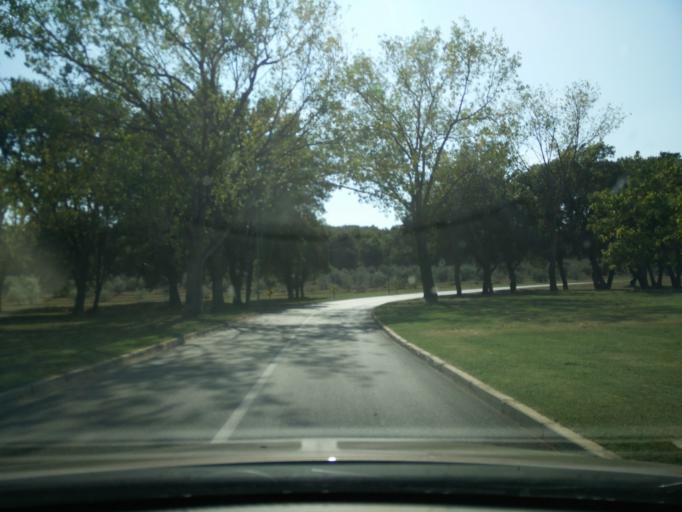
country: HR
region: Istarska
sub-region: Grad Porec
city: Porec
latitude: 45.2017
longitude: 13.6006
